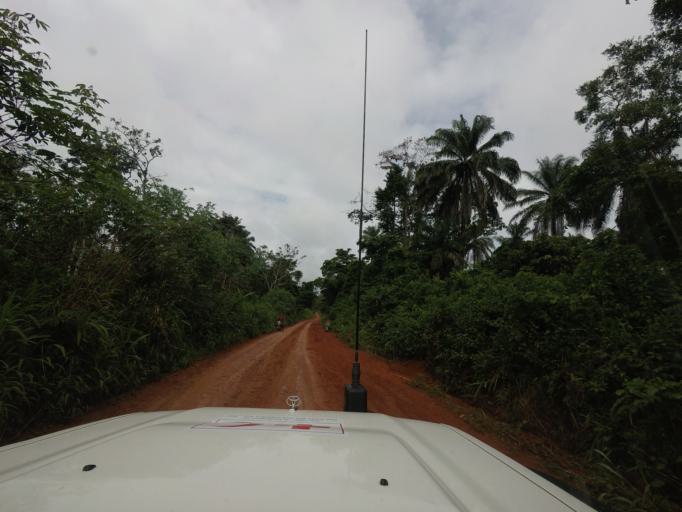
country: GN
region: Nzerekore
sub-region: Nzerekore Prefecture
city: Nzerekore
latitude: 7.7219
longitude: -8.8855
